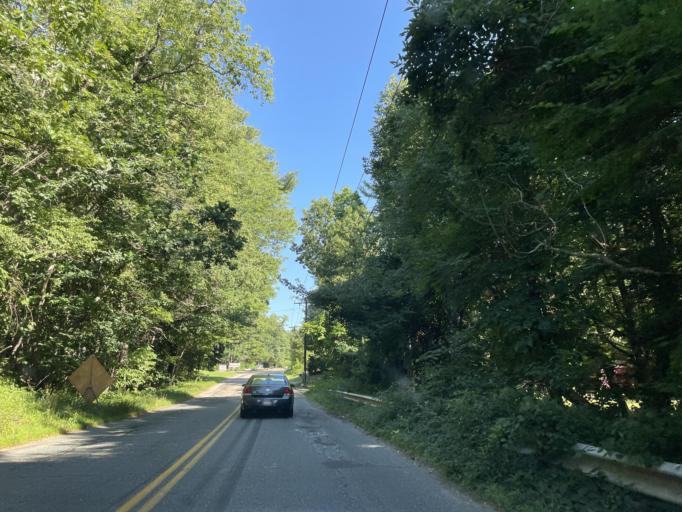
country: US
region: Massachusetts
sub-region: Worcester County
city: East Douglas
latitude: 42.0628
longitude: -71.6923
